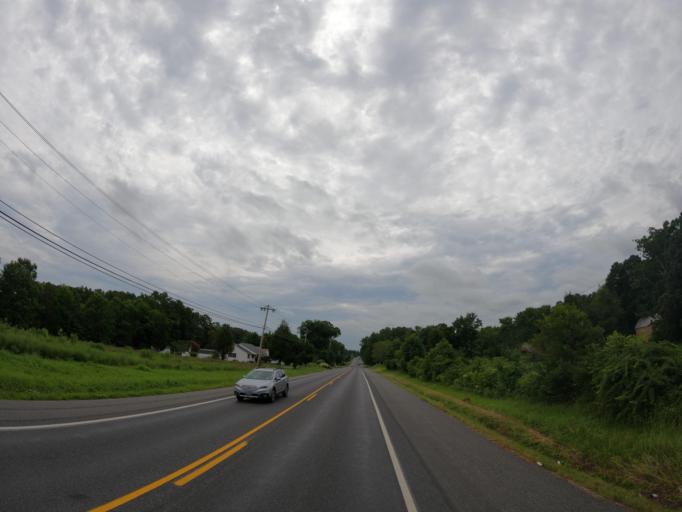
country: US
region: Maryland
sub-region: Saint Mary's County
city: Lexington Park
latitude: 38.2234
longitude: -76.5179
